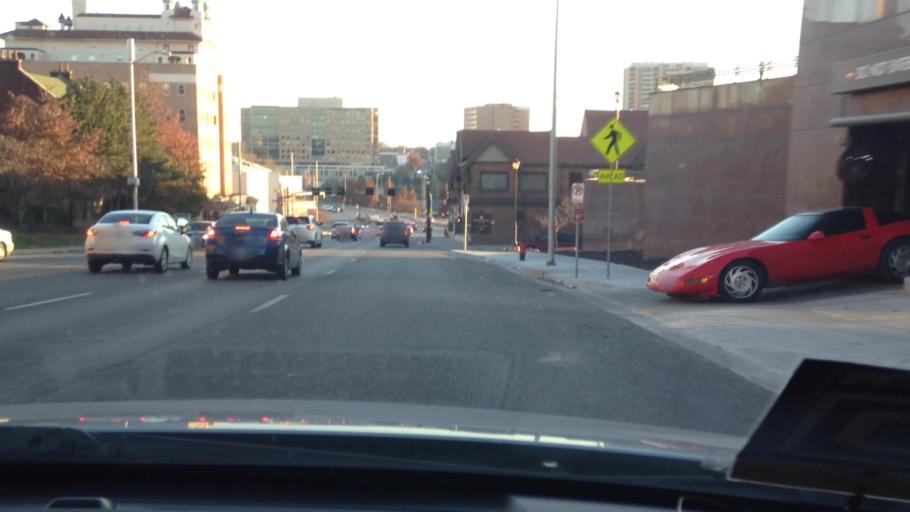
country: US
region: Kansas
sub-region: Johnson County
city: Westwood
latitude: 39.0449
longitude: -94.5869
